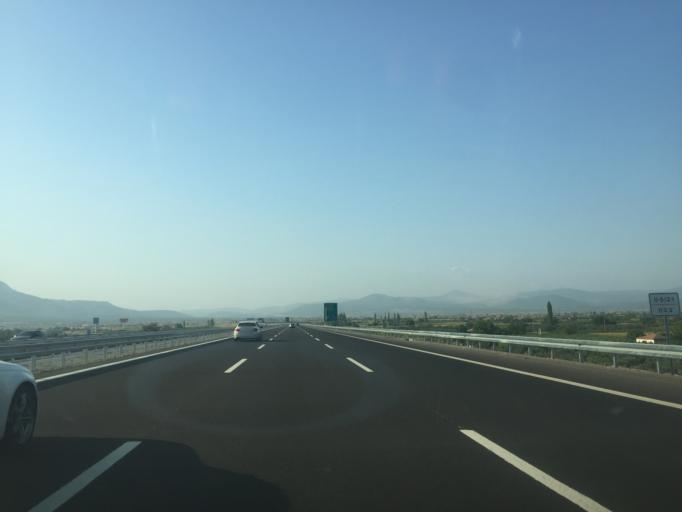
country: TR
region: Manisa
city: Kirkagac
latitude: 39.0801
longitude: 27.7145
